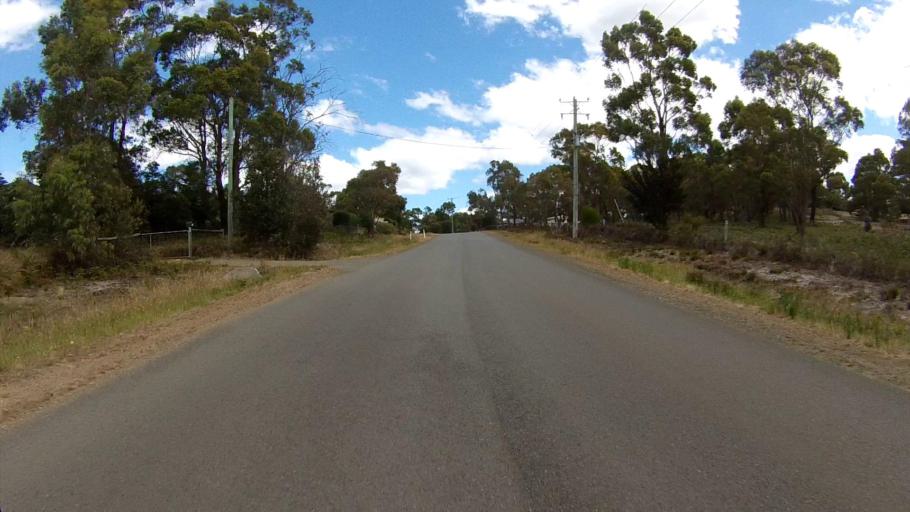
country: AU
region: Tasmania
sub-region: Clarence
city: Acton Park
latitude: -42.8724
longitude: 147.4904
